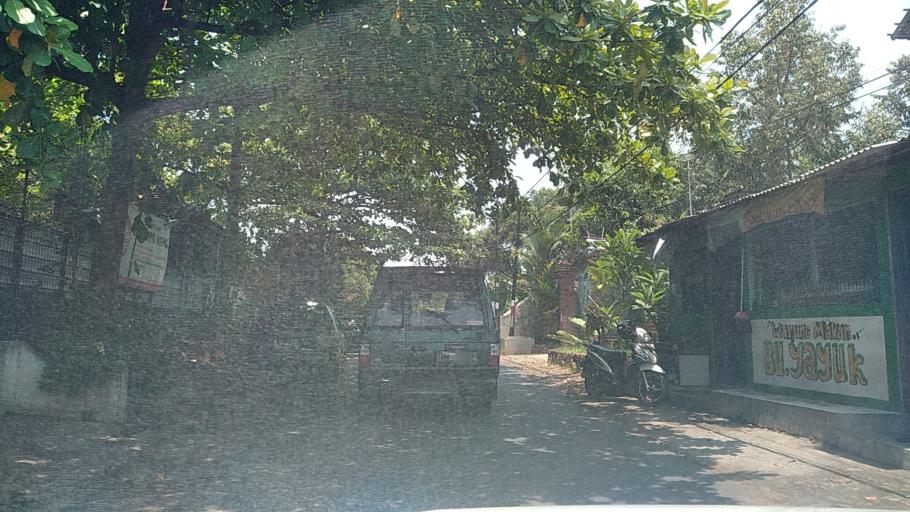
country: ID
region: Central Java
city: Semarang
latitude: -7.0011
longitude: 110.3490
